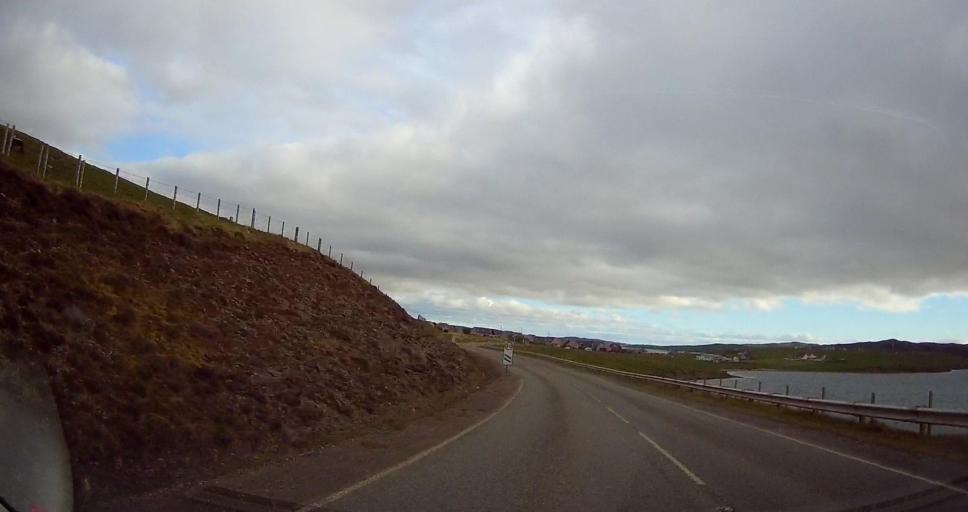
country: GB
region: Scotland
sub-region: Shetland Islands
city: Lerwick
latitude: 60.4041
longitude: -1.3486
